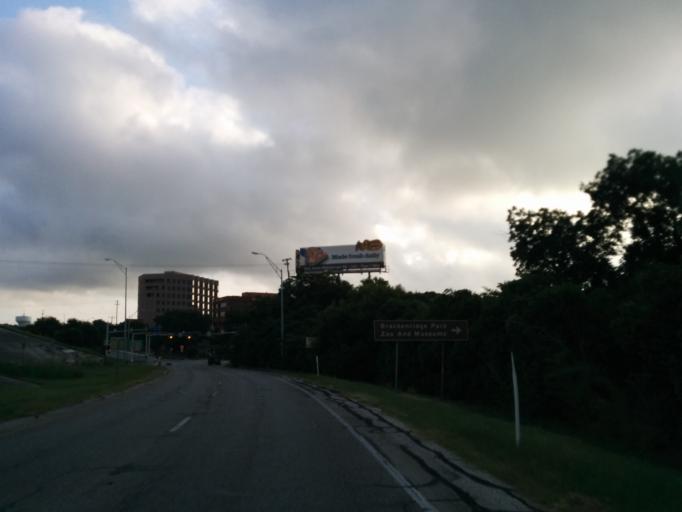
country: US
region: Texas
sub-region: Bexar County
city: Olmos Park
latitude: 29.4541
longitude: -98.4816
